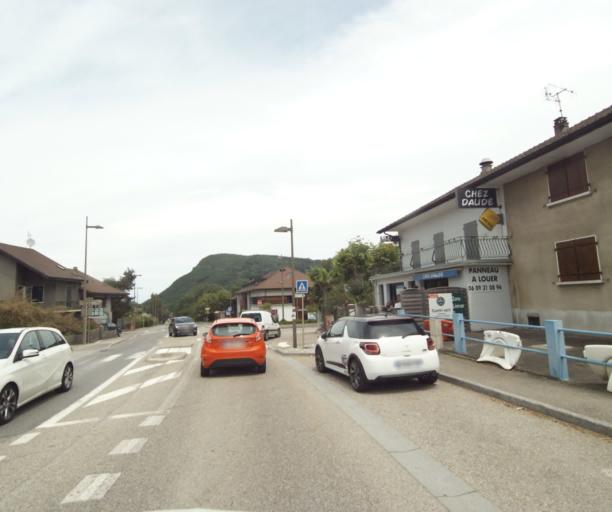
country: FR
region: Rhone-Alpes
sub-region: Departement de la Haute-Savoie
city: Perrignier
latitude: 46.3053
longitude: 6.4386
